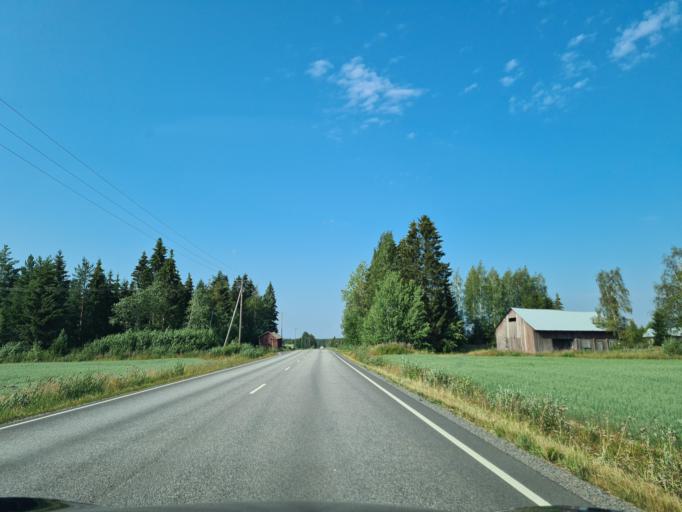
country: FI
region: Satakunta
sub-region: Pohjois-Satakunta
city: Kankaanpaeae
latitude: 61.9126
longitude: 22.5021
